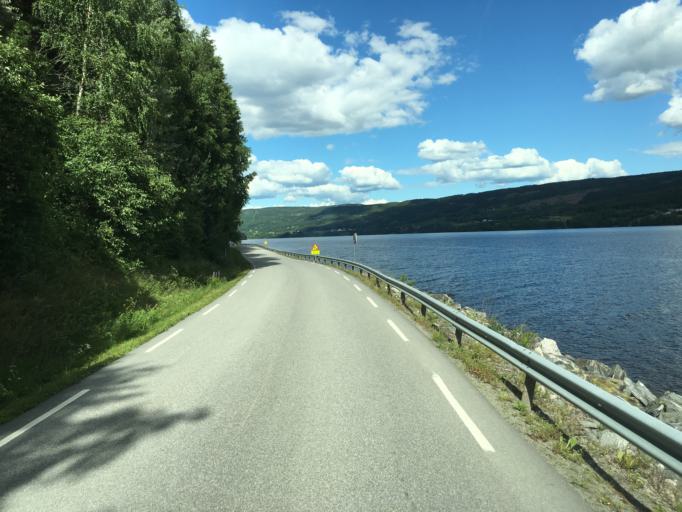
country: NO
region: Oppland
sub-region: Sondre Land
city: Hov
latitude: 60.5991
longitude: 10.3210
